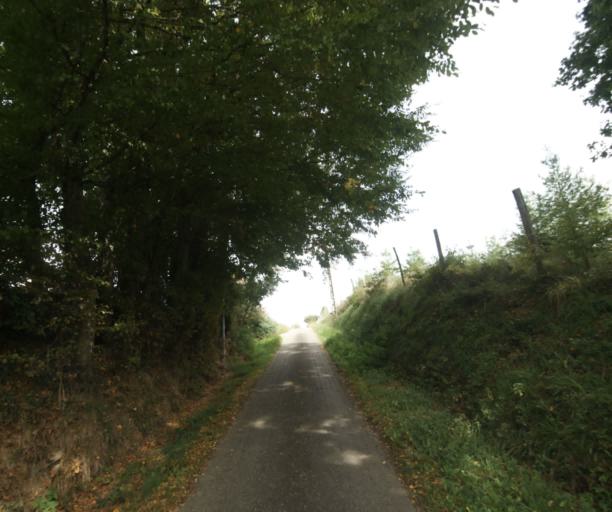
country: FR
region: Midi-Pyrenees
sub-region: Departement du Gers
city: Eauze
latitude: 43.8445
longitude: 0.1050
